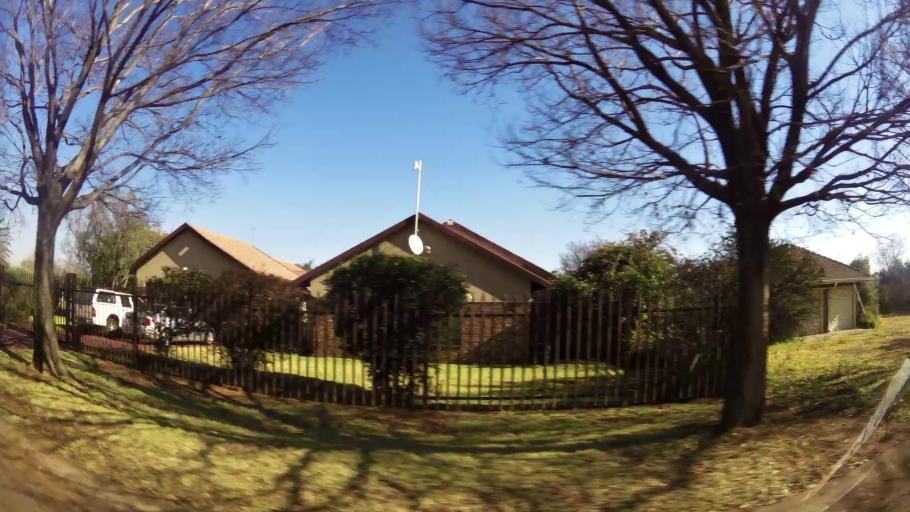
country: ZA
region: Mpumalanga
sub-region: Nkangala District Municipality
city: Witbank
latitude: -25.8910
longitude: 29.2534
